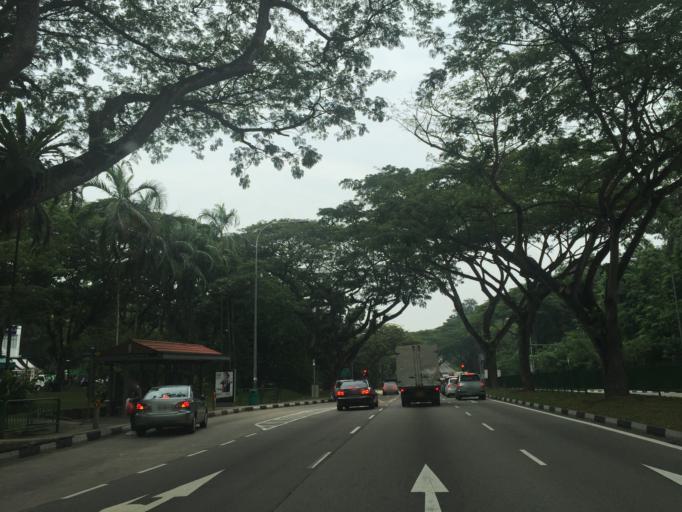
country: SG
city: Singapore
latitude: 1.3830
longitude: 103.8258
